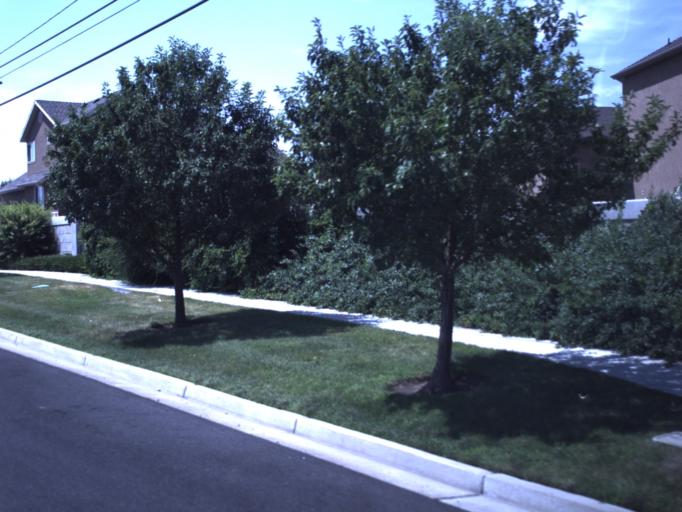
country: US
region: Utah
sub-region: Salt Lake County
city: Kearns
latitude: 40.6617
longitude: -112.0248
